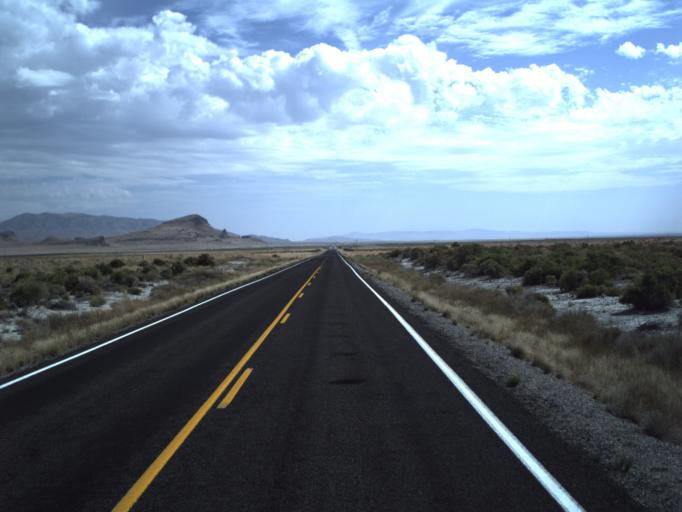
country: US
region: Utah
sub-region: Tooele County
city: Wendover
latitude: 41.4200
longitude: -113.9038
